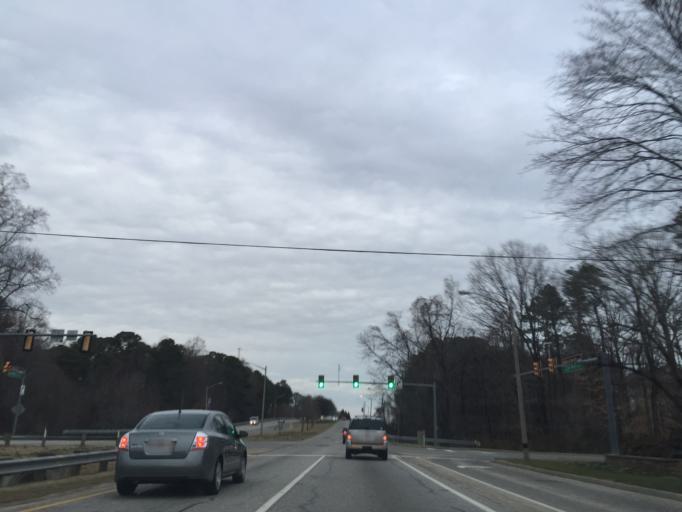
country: US
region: Virginia
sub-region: City of Newport News
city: Newport News
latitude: 37.0669
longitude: -76.4835
